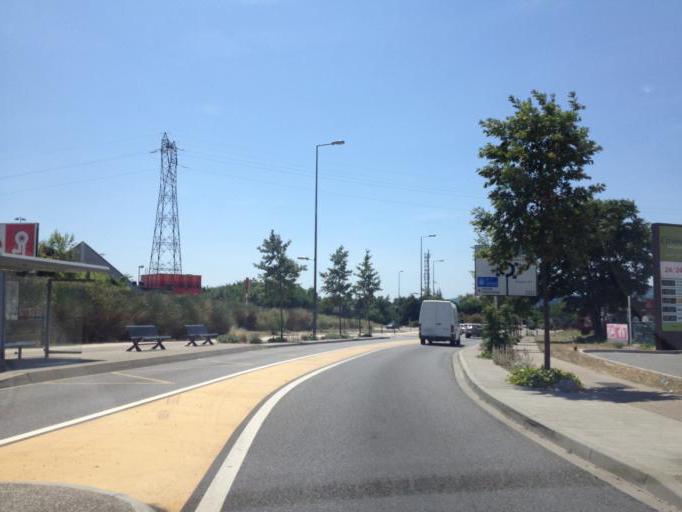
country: FR
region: Rhone-Alpes
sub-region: Departement de l'Ardeche
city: Guilherand-Granges
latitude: 44.9067
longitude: 4.8798
